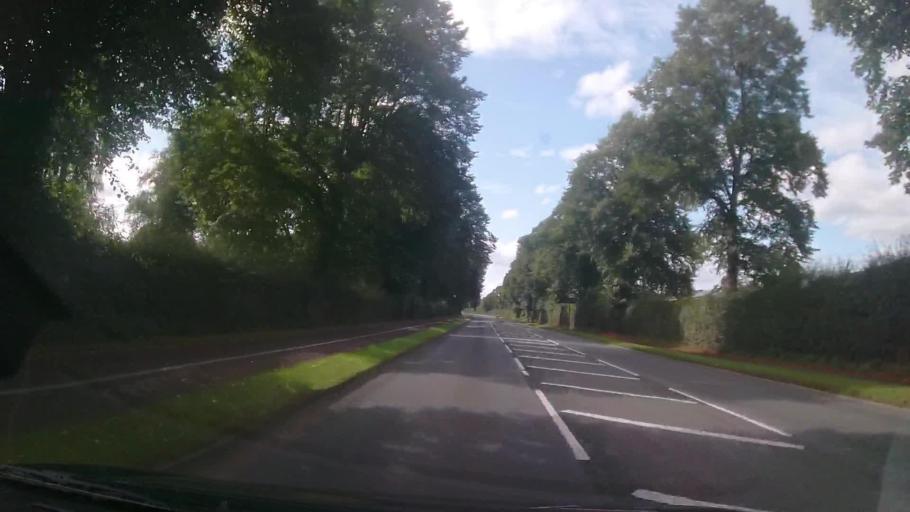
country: GB
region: England
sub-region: Shropshire
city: Shrewsbury
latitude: 52.7117
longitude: -2.7840
